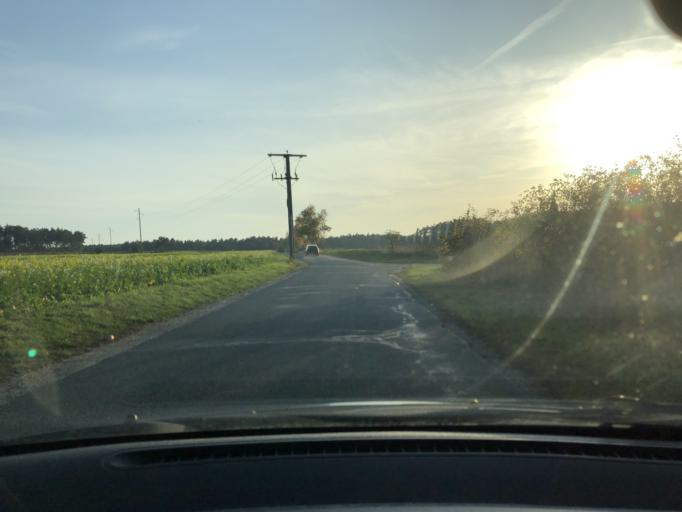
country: DE
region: Lower Saxony
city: Hitzacker
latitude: 53.1360
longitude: 11.0309
